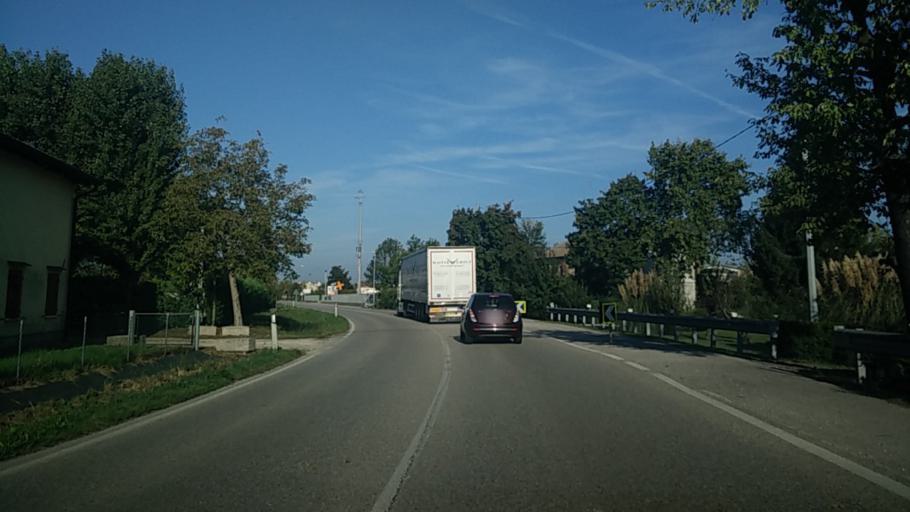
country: IT
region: Veneto
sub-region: Provincia di Padova
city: Trebaseleghe
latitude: 45.5816
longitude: 12.0657
